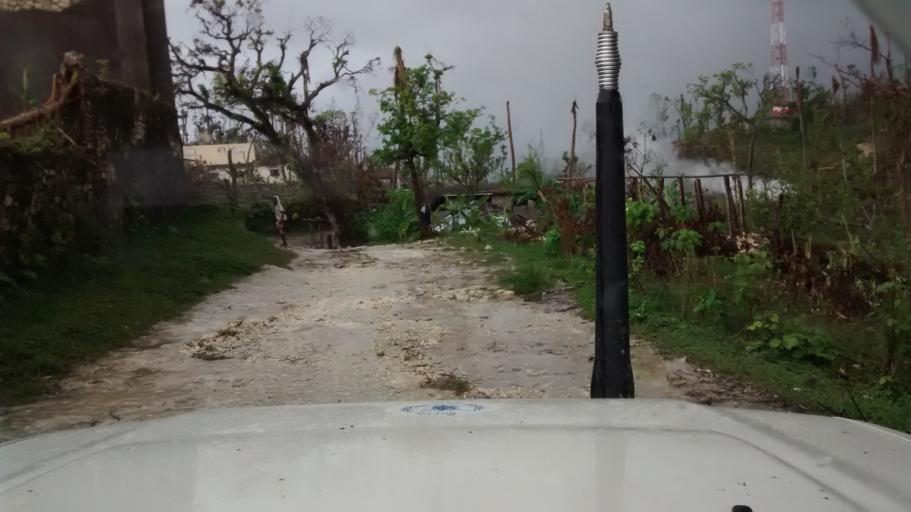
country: HT
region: Grandans
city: Moron
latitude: 18.5361
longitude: -74.1563
